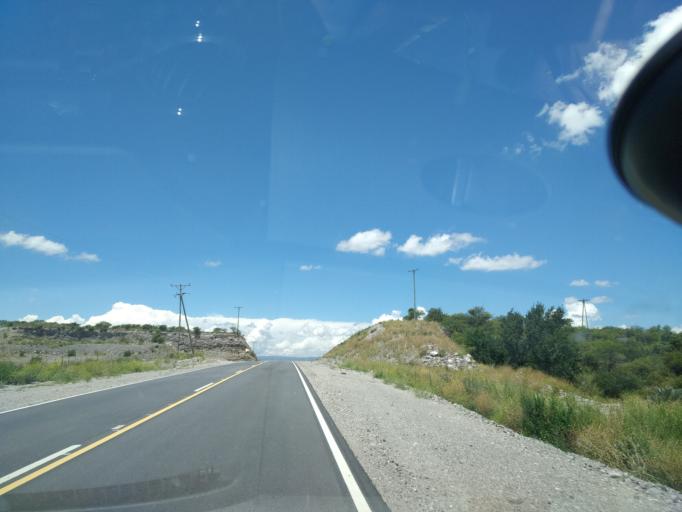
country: AR
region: Cordoba
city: Salsacate
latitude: -31.3639
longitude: -65.2060
